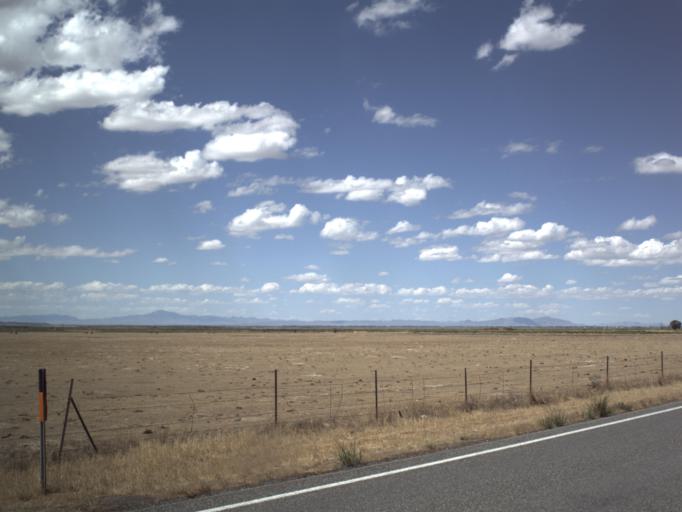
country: US
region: Utah
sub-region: Millard County
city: Delta
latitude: 39.2049
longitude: -112.4107
